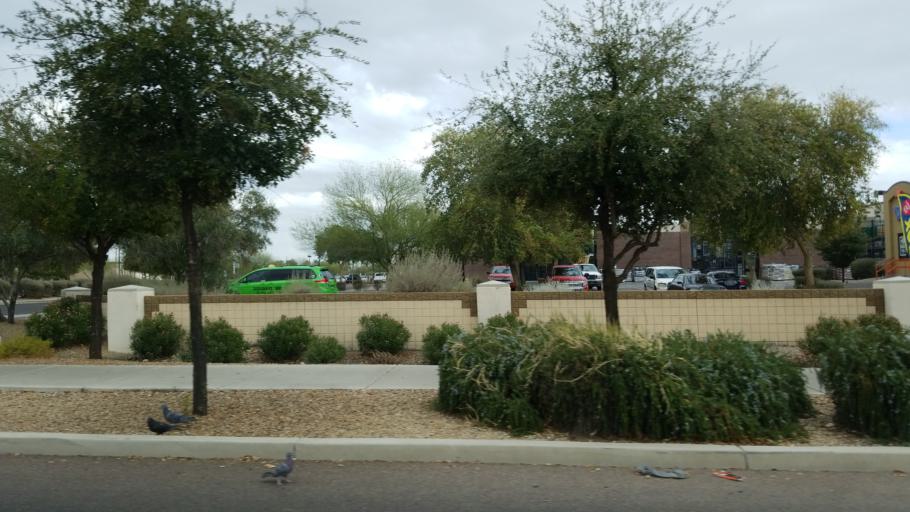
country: US
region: Arizona
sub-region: Maricopa County
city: Glendale
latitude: 33.5513
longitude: -112.1861
